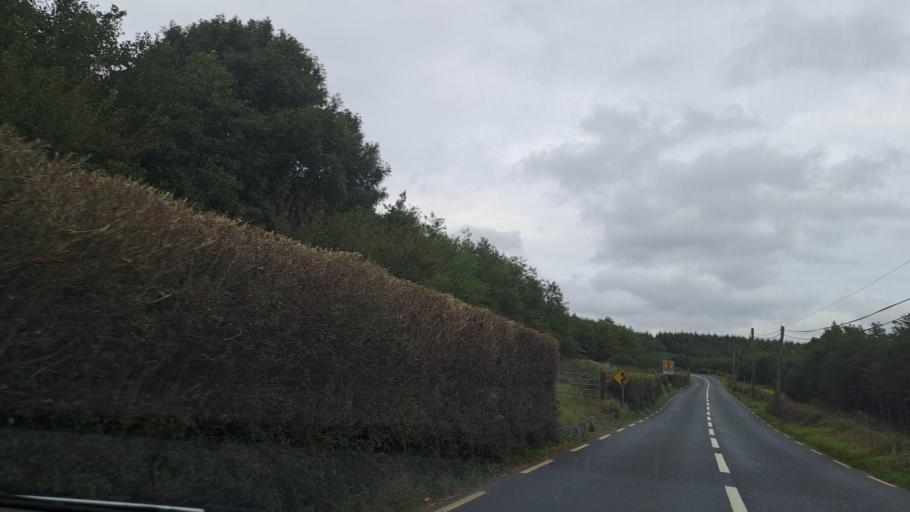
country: IE
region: Ulster
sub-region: An Cabhan
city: Bailieborough
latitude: 53.9301
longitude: -6.9673
